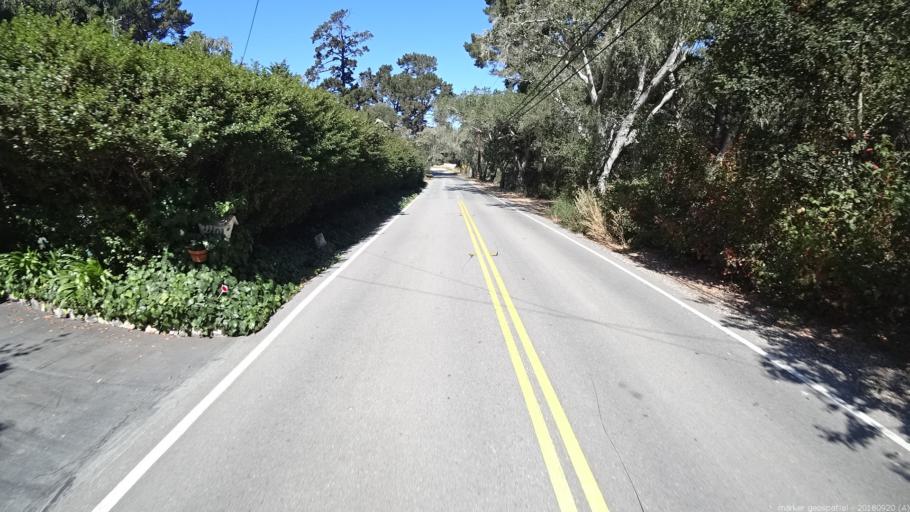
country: US
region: California
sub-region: Monterey County
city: Monterey
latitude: 36.5923
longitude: -121.8703
